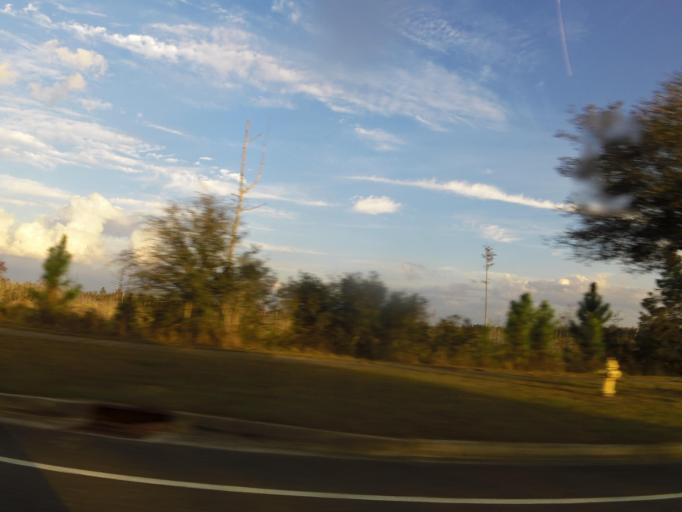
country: US
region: Florida
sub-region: Duval County
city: Baldwin
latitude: 30.2697
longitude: -81.8863
